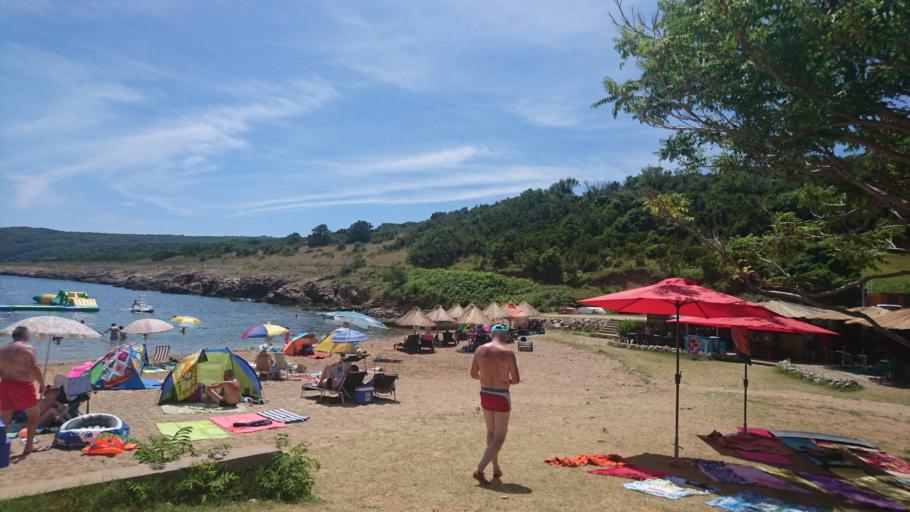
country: HR
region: Primorsko-Goranska
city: Selce
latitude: 45.1055
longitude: 14.6646
